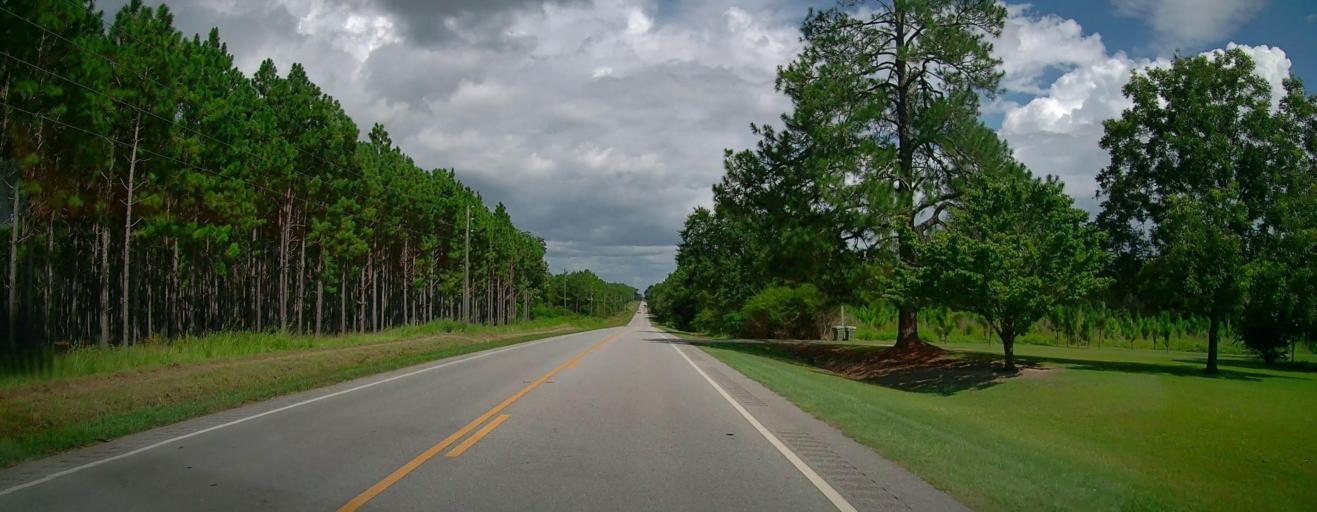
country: US
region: Georgia
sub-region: Coffee County
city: Broxton
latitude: 31.5767
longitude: -83.0474
